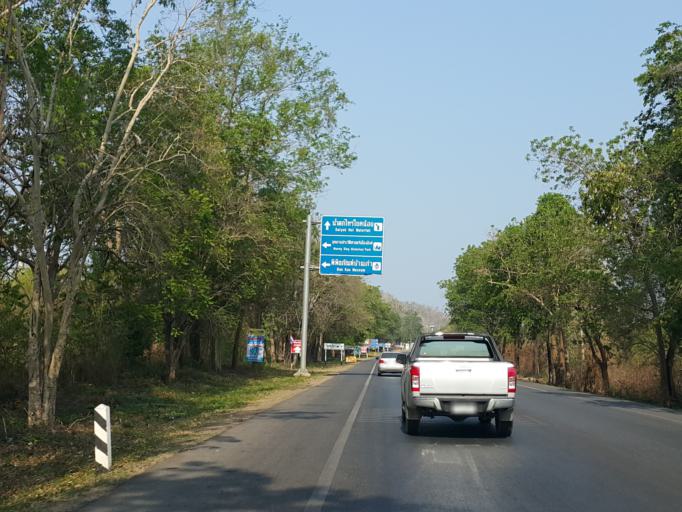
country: TH
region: Kanchanaburi
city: Sai Yok
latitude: 14.0898
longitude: 99.2843
